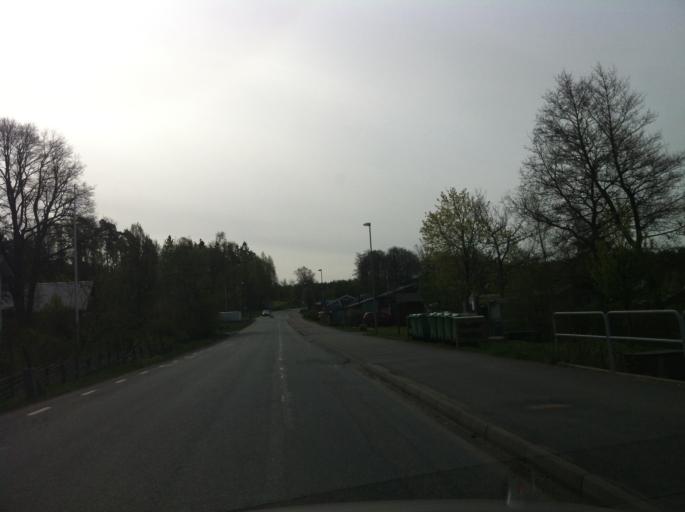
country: SE
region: Vaestra Goetaland
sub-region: Marks Kommun
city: Kinna
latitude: 57.4708
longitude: 12.7112
